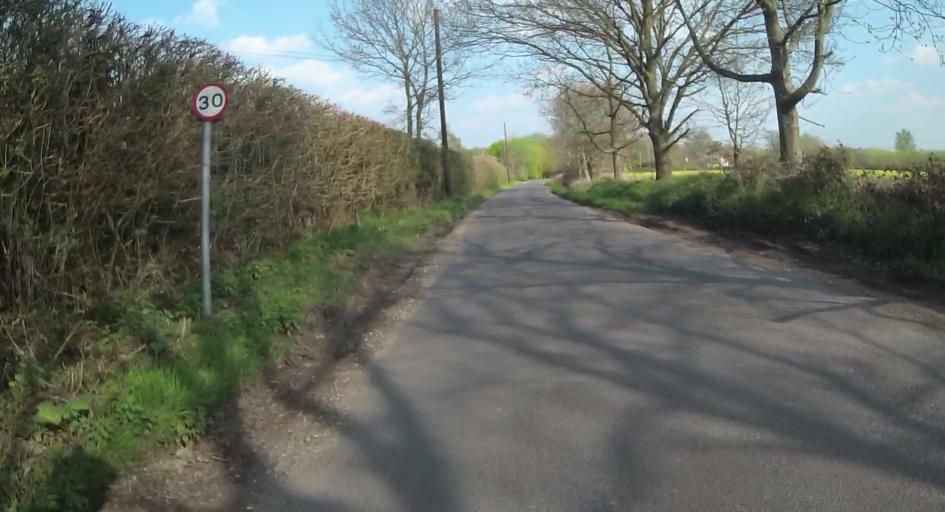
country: GB
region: England
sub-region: Hampshire
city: Tadley
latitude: 51.3468
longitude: -1.0787
